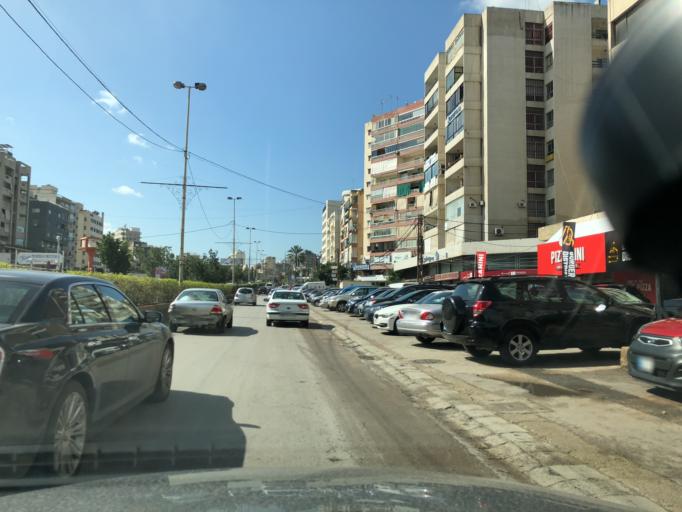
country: LB
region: Mont-Liban
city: Jdaidet el Matn
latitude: 33.8805
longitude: 35.5527
